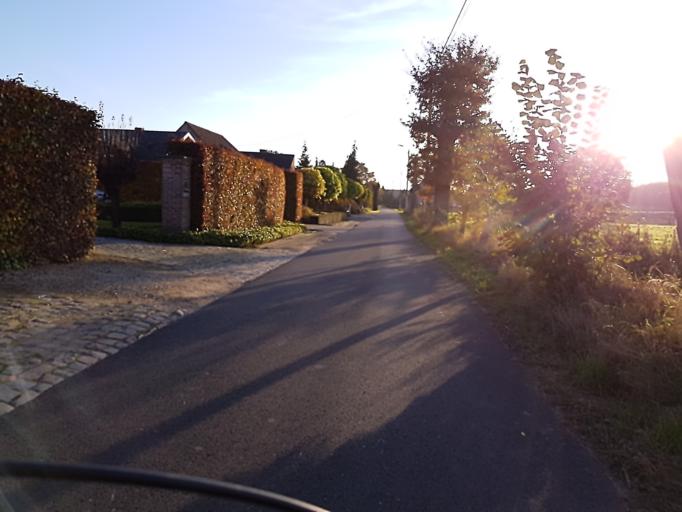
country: BE
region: Flanders
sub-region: Provincie Antwerpen
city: Bonheiden
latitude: 51.0434
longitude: 4.5801
